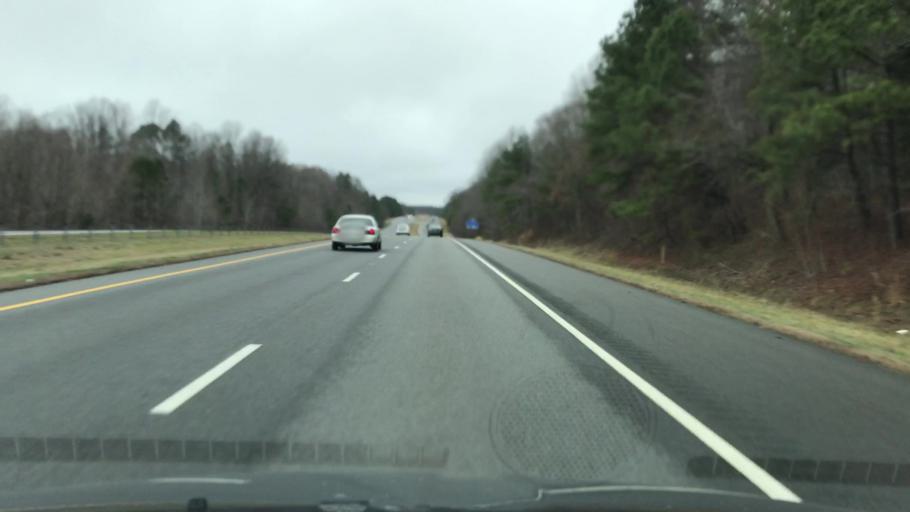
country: US
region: Maryland
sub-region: Calvert County
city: Long Beach
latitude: 38.4544
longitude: -76.4974
